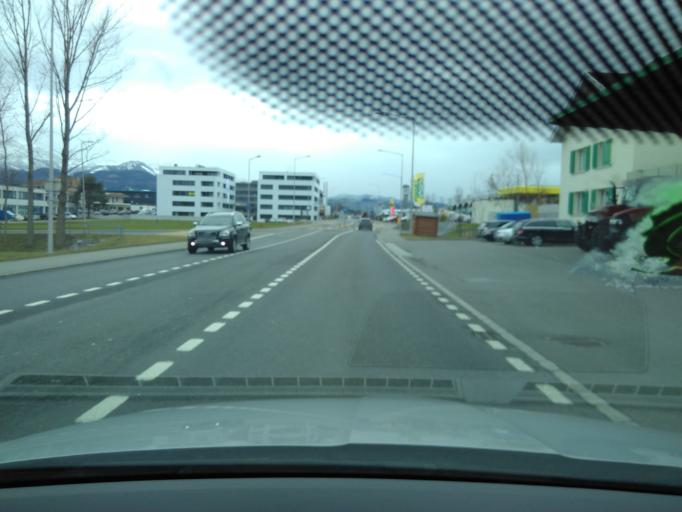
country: CH
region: Lucerne
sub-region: Hochdorf District
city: Emmen
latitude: 47.0933
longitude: 8.2551
